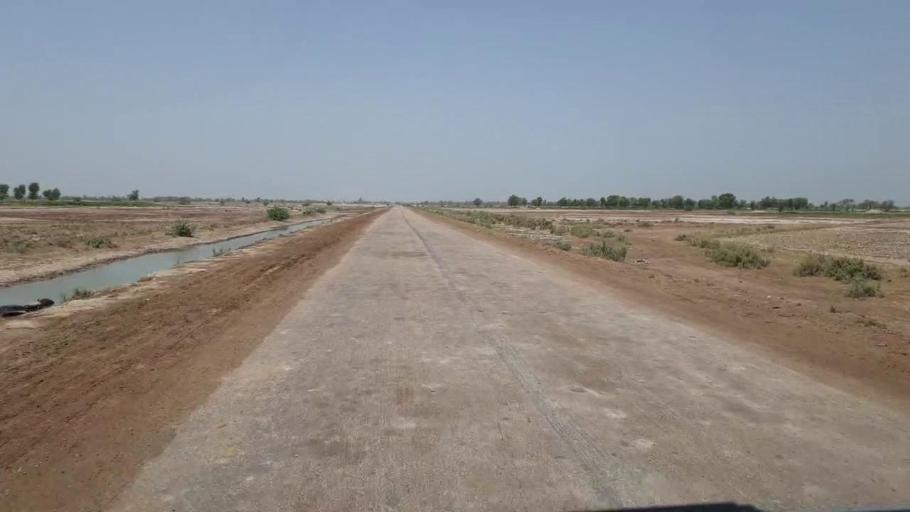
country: PK
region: Sindh
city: Nawabshah
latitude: 26.3664
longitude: 68.4119
